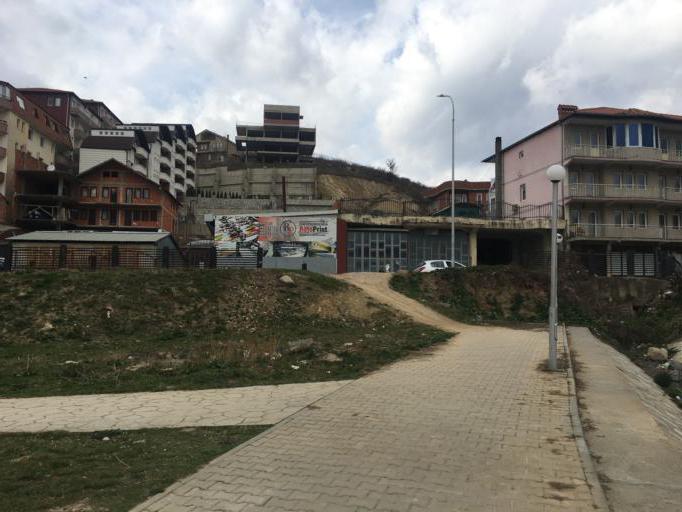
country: XK
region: Pristina
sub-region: Komuna e Prishtines
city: Pristina
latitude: 42.6677
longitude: 21.1882
